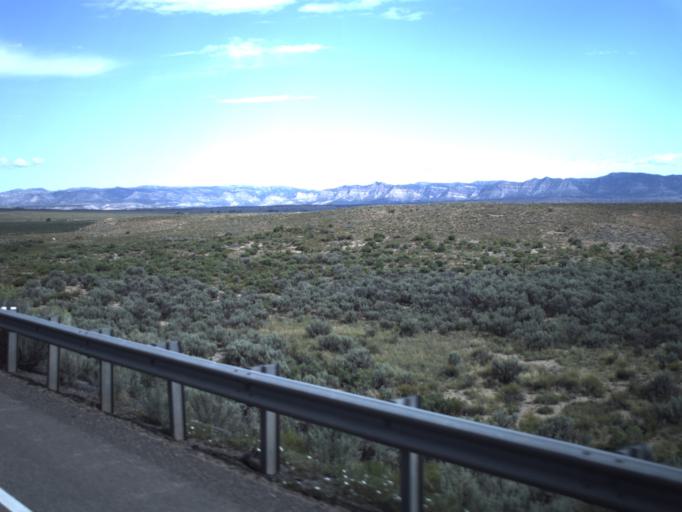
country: US
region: Utah
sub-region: Carbon County
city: East Carbon City
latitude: 39.5203
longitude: -110.5607
